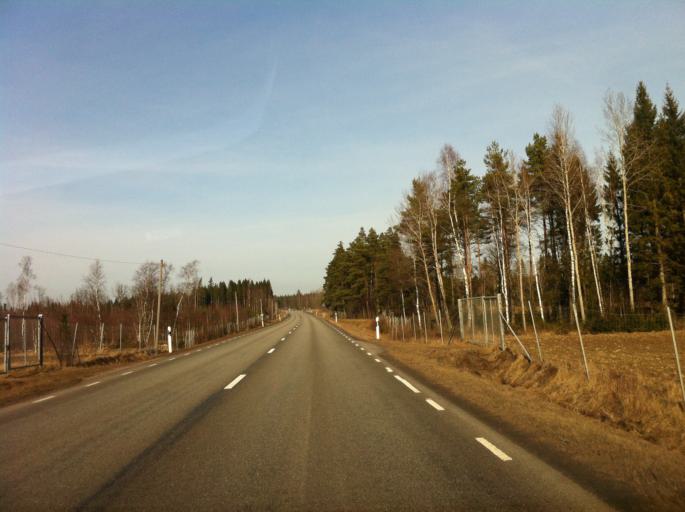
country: SE
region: Vaestra Goetaland
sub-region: Tidaholms Kommun
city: Tidaholm
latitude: 58.1648
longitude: 13.9048
